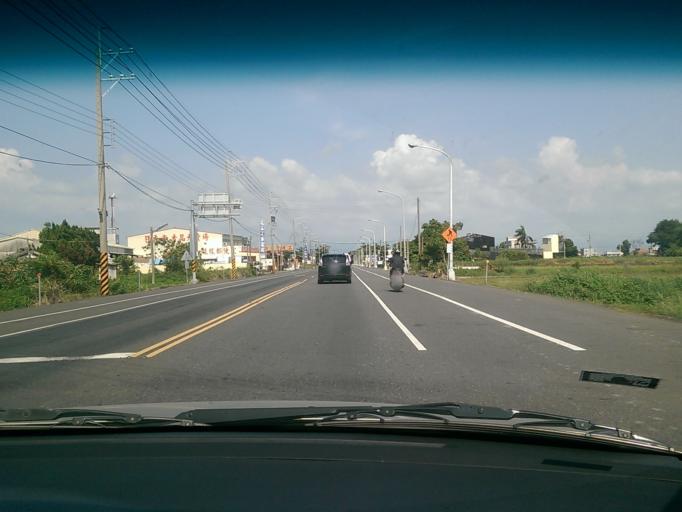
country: TW
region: Taiwan
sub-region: Chiayi
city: Taibao
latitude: 23.5610
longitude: 120.3158
